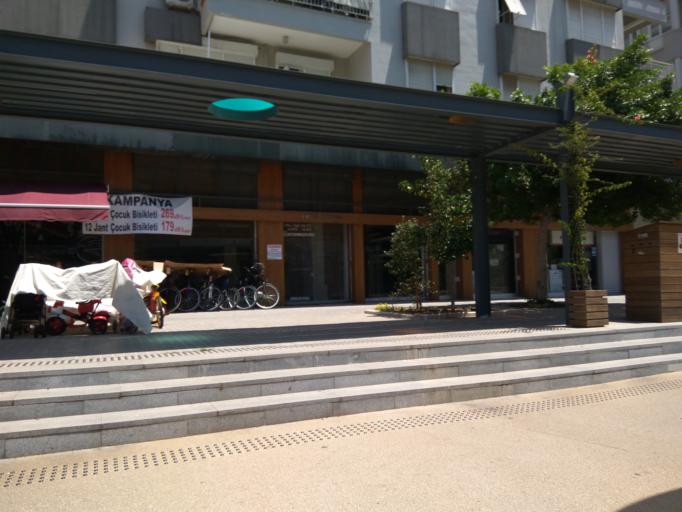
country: TR
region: Antalya
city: Antalya
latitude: 36.8981
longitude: 30.6961
